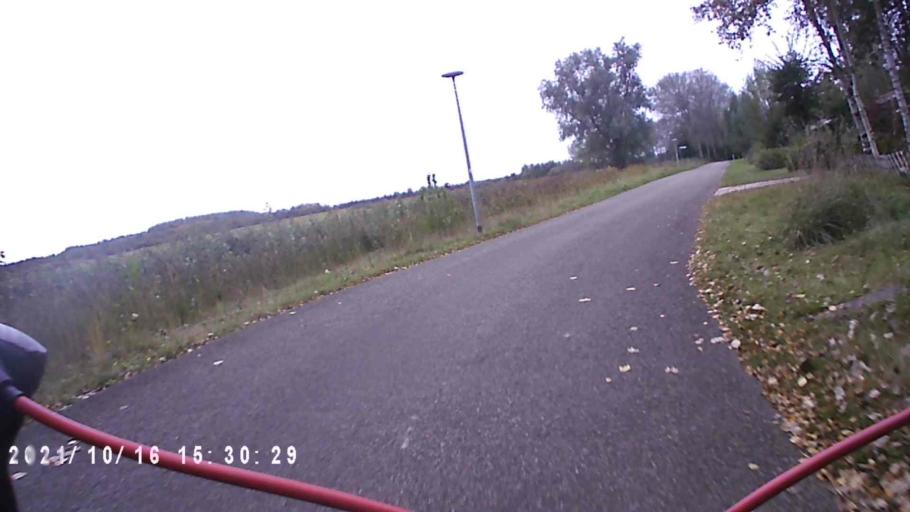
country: NL
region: Friesland
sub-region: Gemeente Dongeradeel
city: Anjum
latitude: 53.4038
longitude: 6.2208
